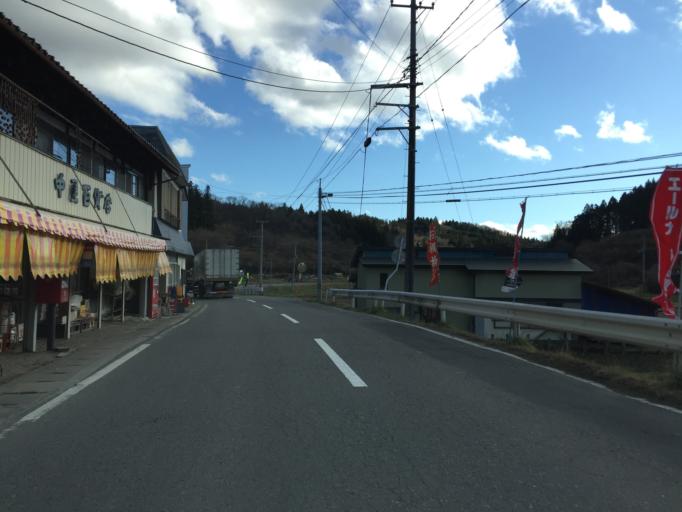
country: JP
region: Fukushima
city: Funehikimachi-funehiki
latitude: 37.5059
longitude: 140.5783
